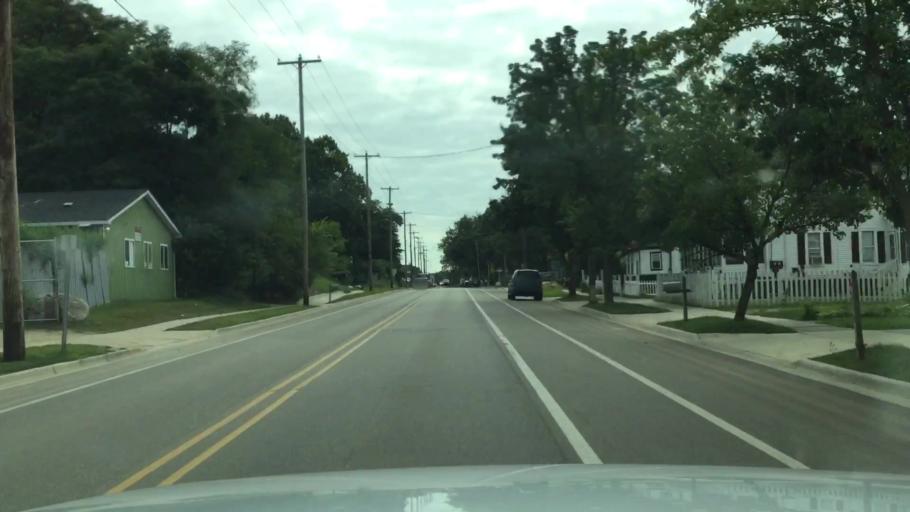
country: US
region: Michigan
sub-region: Kalamazoo County
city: Eastwood
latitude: 42.2945
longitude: -85.5634
